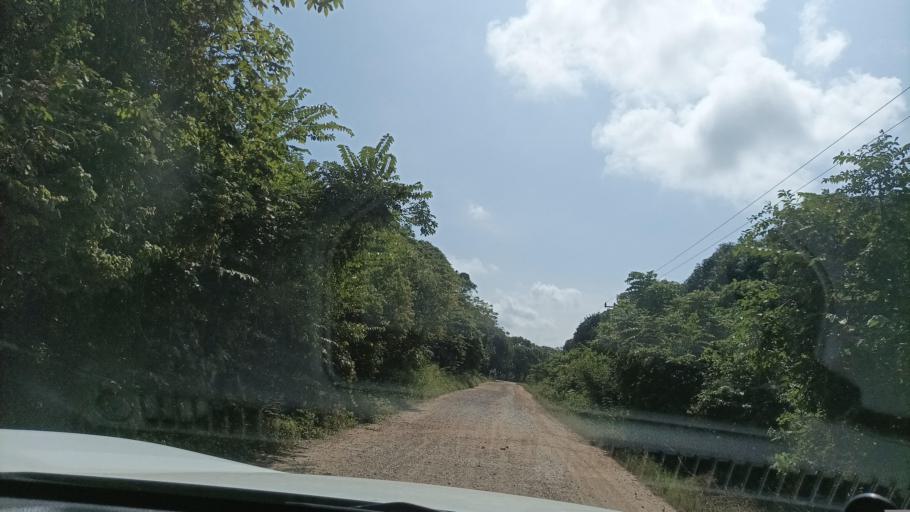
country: MX
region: Veracruz
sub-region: Chinameca
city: Chacalapa
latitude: 18.1231
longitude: -94.6548
